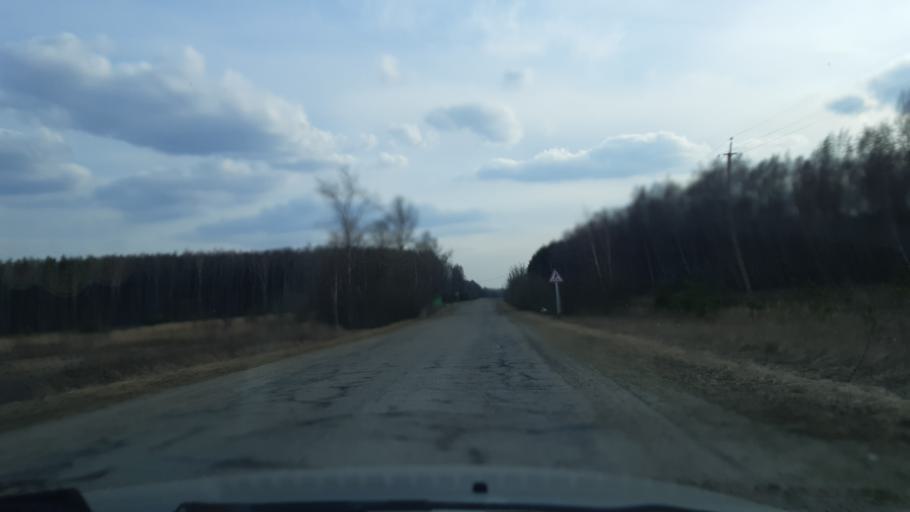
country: RU
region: Vladimir
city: Nikologory
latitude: 56.1204
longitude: 41.9866
